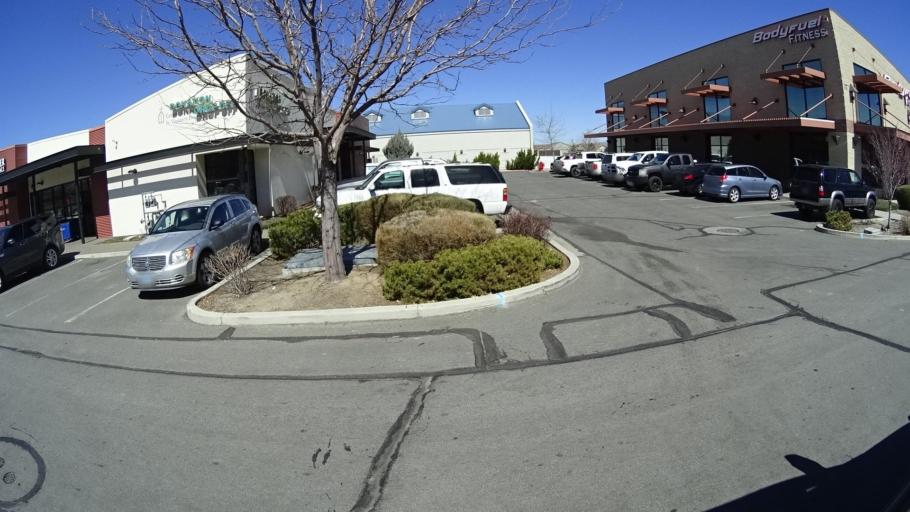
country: US
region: Nevada
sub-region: Washoe County
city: Sparks
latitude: 39.5777
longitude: -119.7231
